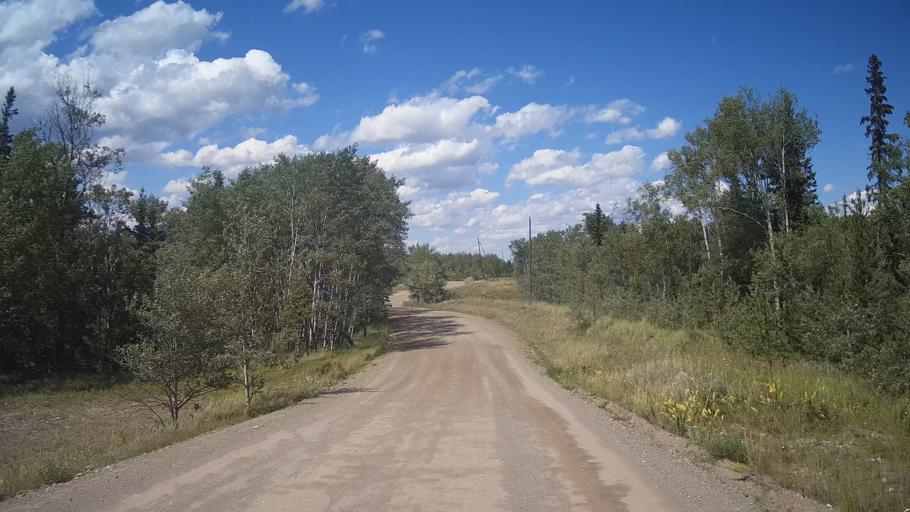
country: CA
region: British Columbia
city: Cache Creek
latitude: 51.2597
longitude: -121.6910
